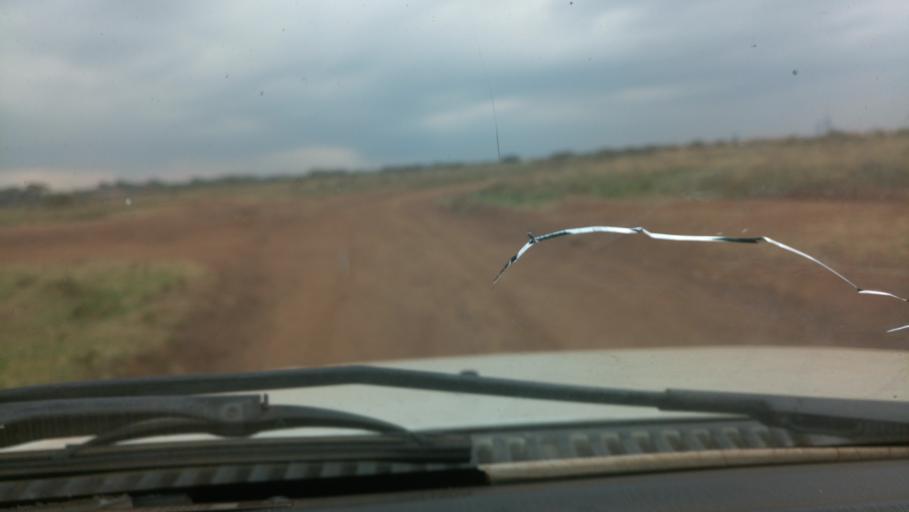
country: KE
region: Nairobi Area
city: Nairobi
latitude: -1.3385
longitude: 36.8108
